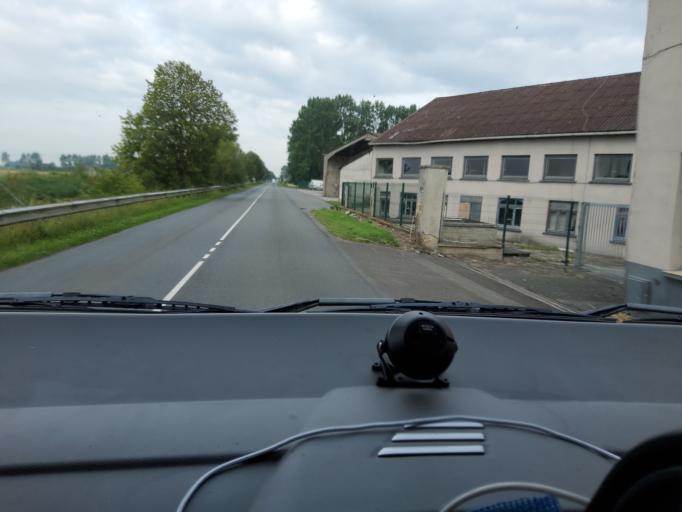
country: FR
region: Nord-Pas-de-Calais
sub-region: Departement du Nord
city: Bierne
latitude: 50.9706
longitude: 2.4080
